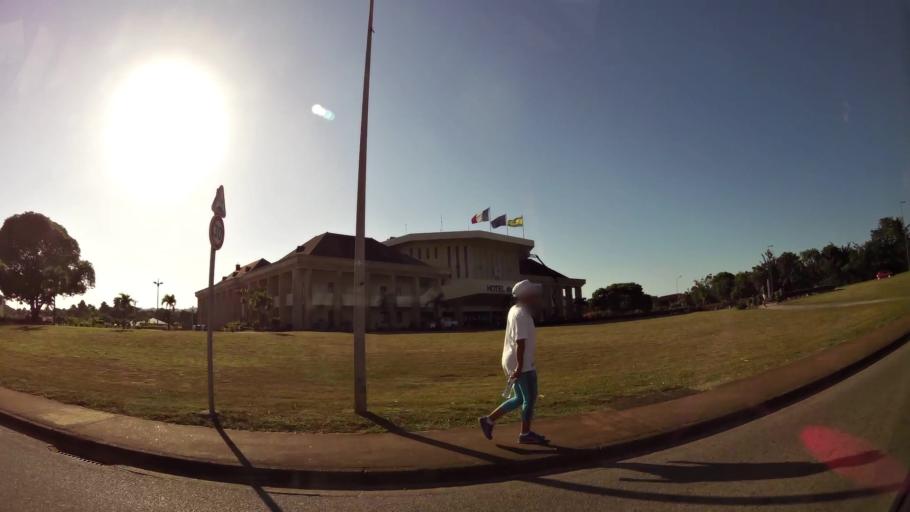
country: GF
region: Guyane
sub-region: Guyane
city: Remire-Montjoly
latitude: 4.9045
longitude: -52.2759
